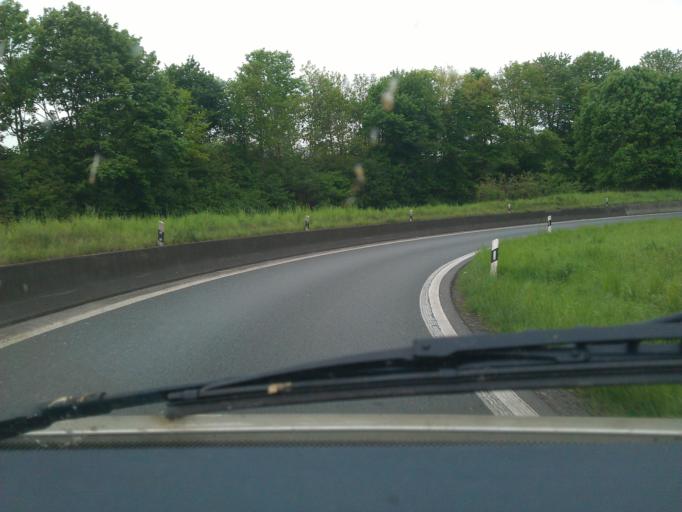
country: DE
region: North Rhine-Westphalia
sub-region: Regierungsbezirk Munster
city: Bottrop
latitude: 51.5540
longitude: 6.9273
